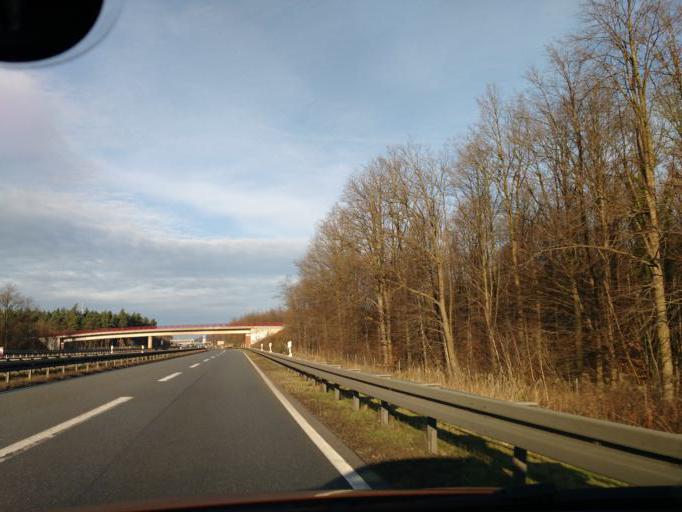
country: DE
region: Lower Saxony
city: Lehrte
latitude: 52.4006
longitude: 9.8998
